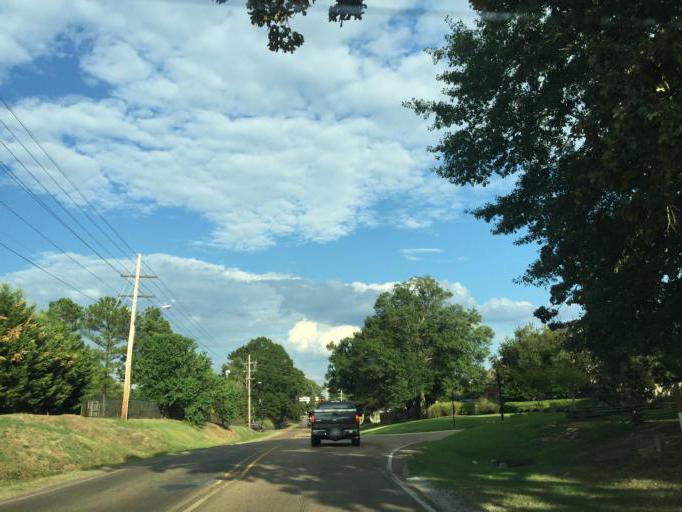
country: US
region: Mississippi
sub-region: Madison County
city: Madison
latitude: 32.4651
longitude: -90.0928
